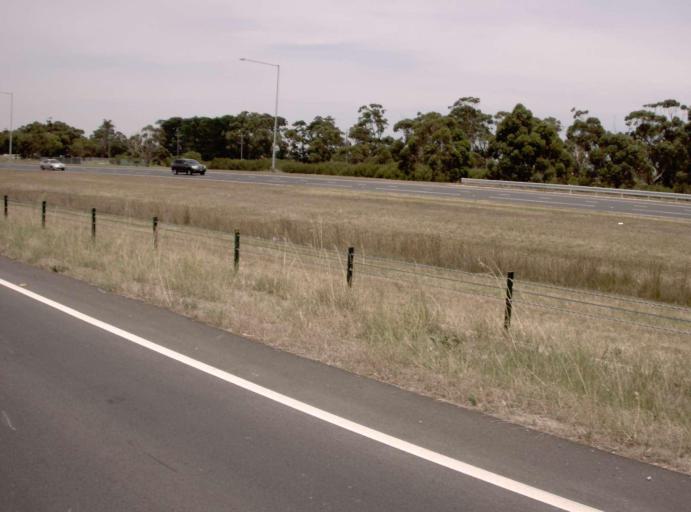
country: AU
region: Victoria
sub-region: Kingston
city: Carrum
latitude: -38.0842
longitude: 145.1491
